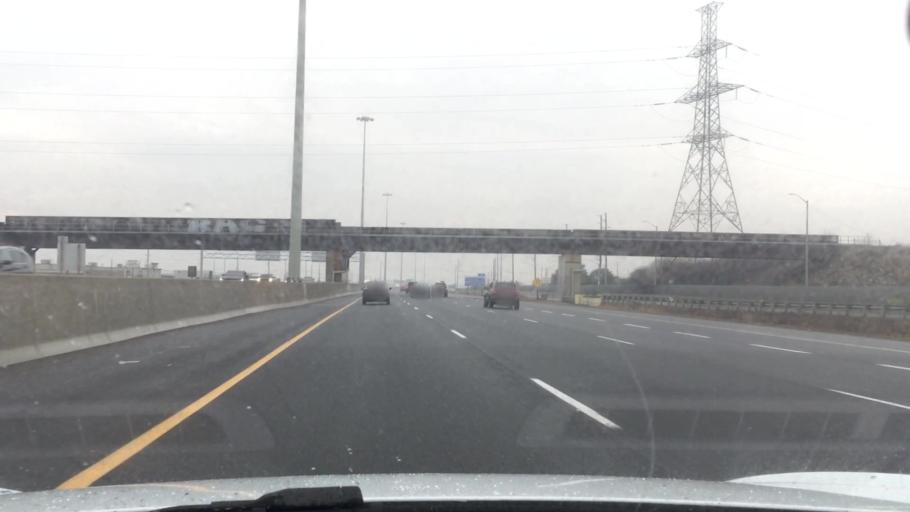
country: CA
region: Ontario
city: Oshawa
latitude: 43.8750
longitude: -78.8797
